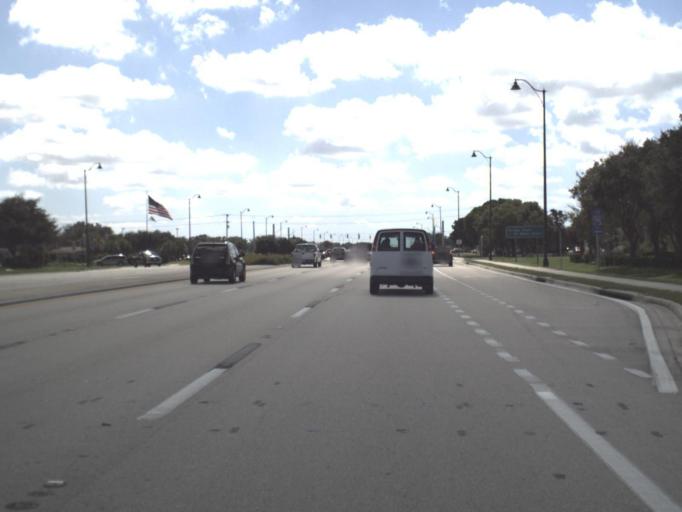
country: US
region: Florida
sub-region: Lee County
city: Bonita Springs
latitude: 26.3338
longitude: -81.8063
